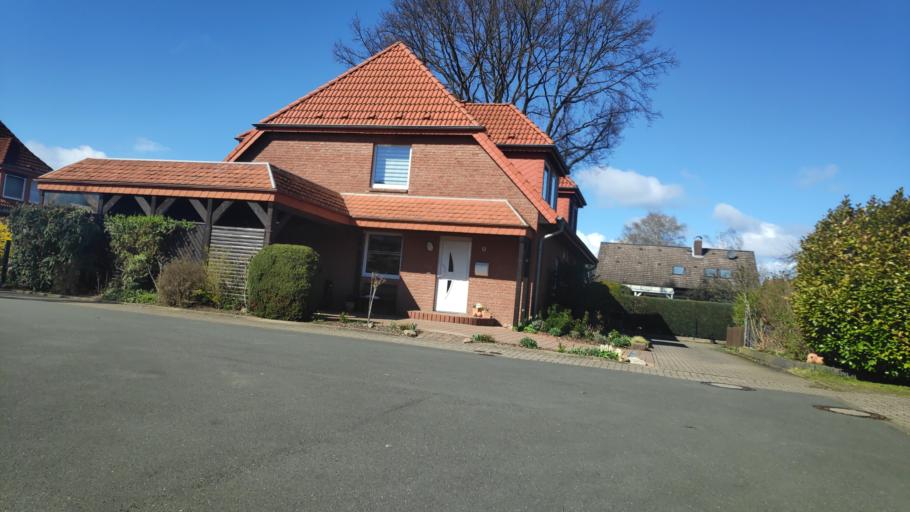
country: DE
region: North Rhine-Westphalia
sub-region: Regierungsbezirk Detmold
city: Minden
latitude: 52.3091
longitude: 8.9102
